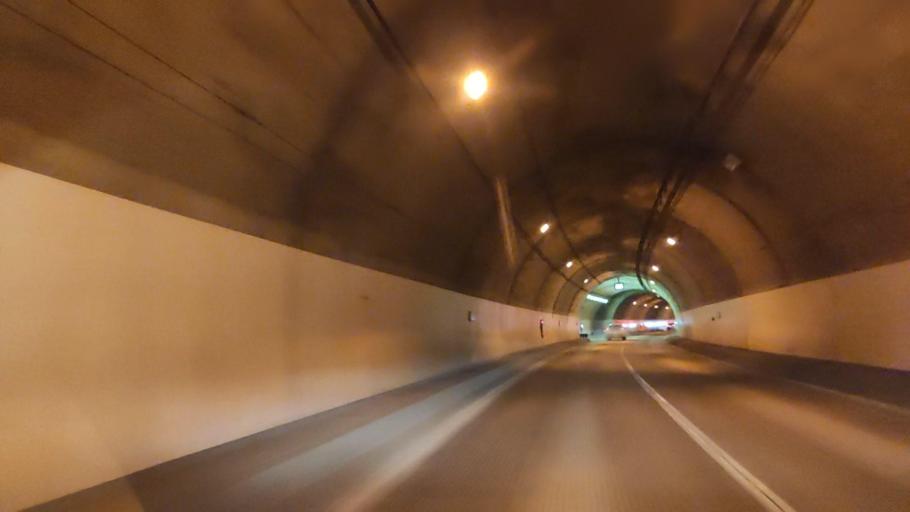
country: JP
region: Hokkaido
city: Ishikari
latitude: 43.4551
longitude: 141.4091
